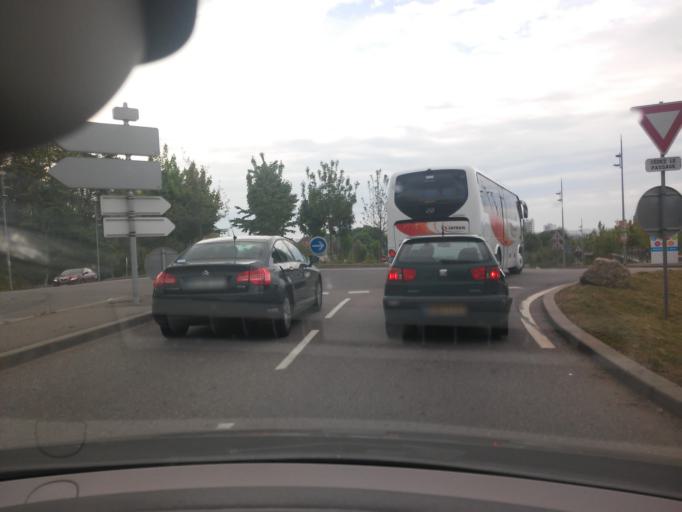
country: FR
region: Lorraine
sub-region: Departement de Meurthe-et-Moselle
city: Laxou
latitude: 48.7013
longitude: 6.1357
